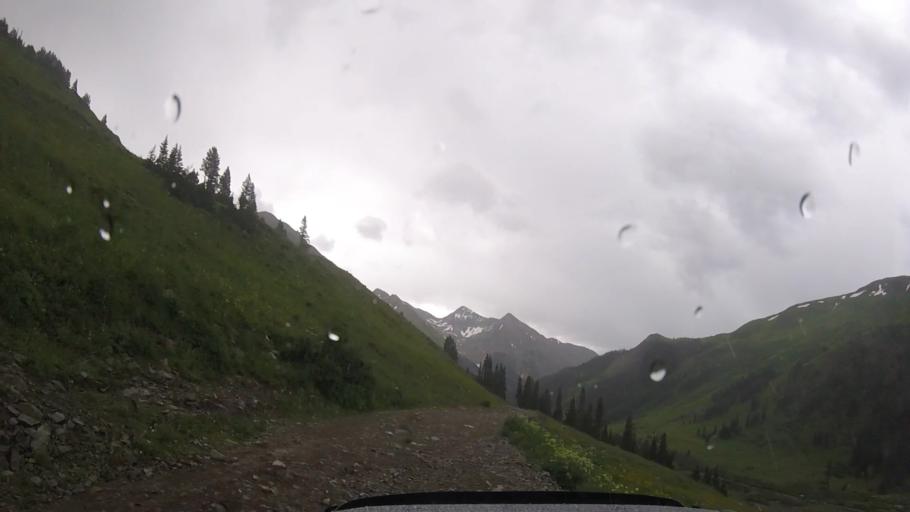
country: US
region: Colorado
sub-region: Ouray County
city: Ouray
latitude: 37.9332
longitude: -107.5682
